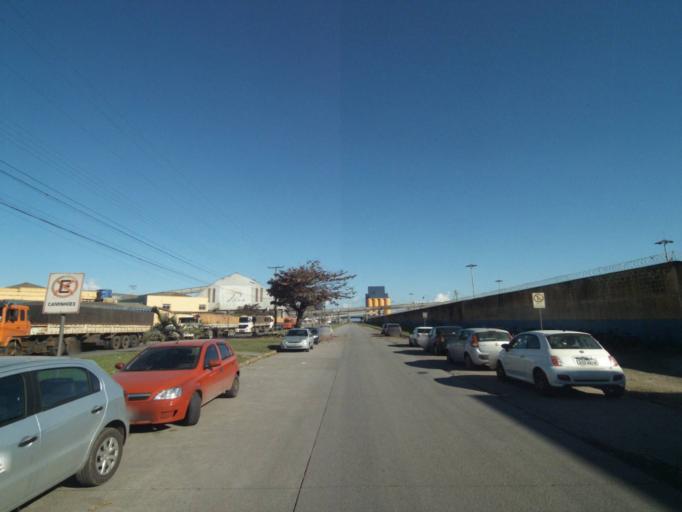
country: BR
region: Parana
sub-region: Paranagua
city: Paranagua
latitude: -25.5036
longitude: -48.5197
